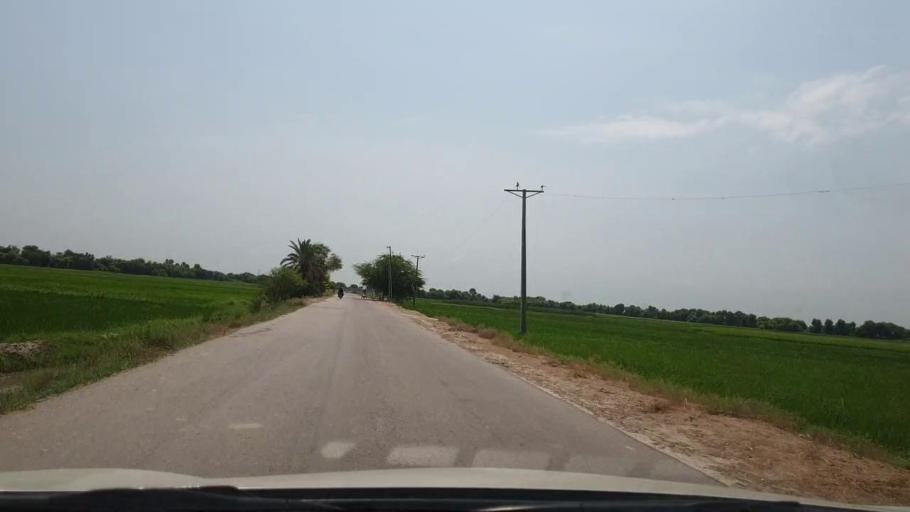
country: PK
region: Sindh
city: Ratodero
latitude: 27.8200
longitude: 68.2451
